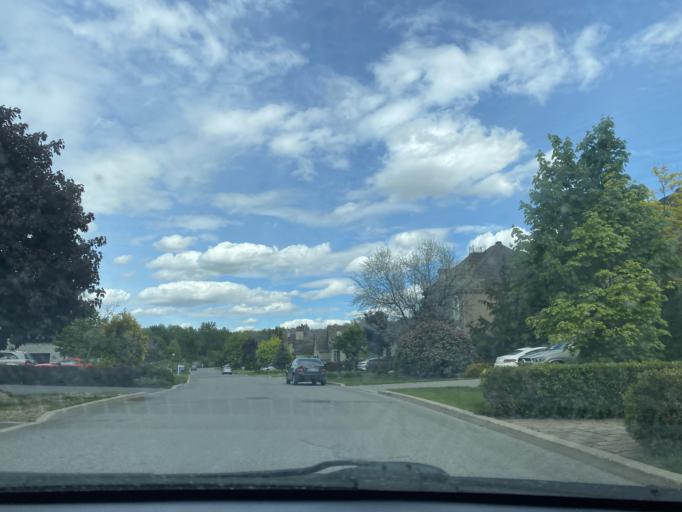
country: CA
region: Quebec
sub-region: Monteregie
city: Carignan
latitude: 45.4729
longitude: -73.2930
